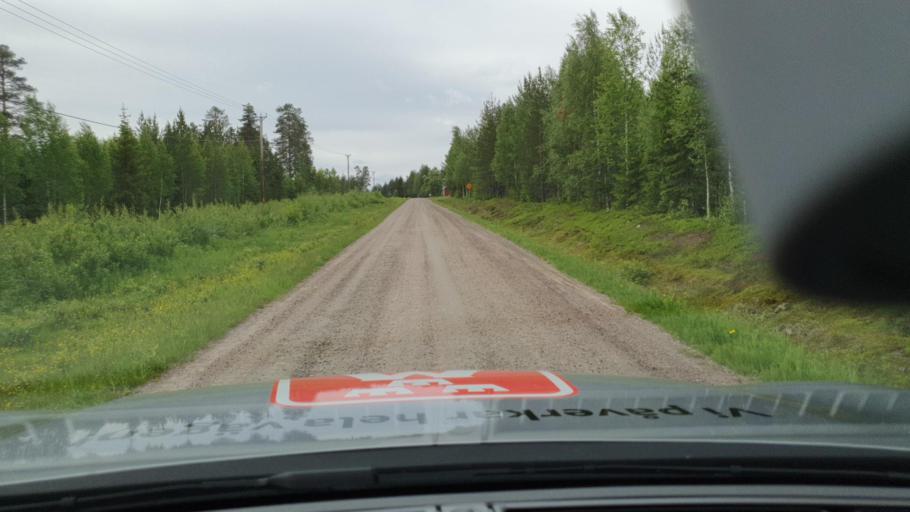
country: SE
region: Norrbotten
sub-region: Kalix Kommun
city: Kalix
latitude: 66.0318
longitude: 23.4397
